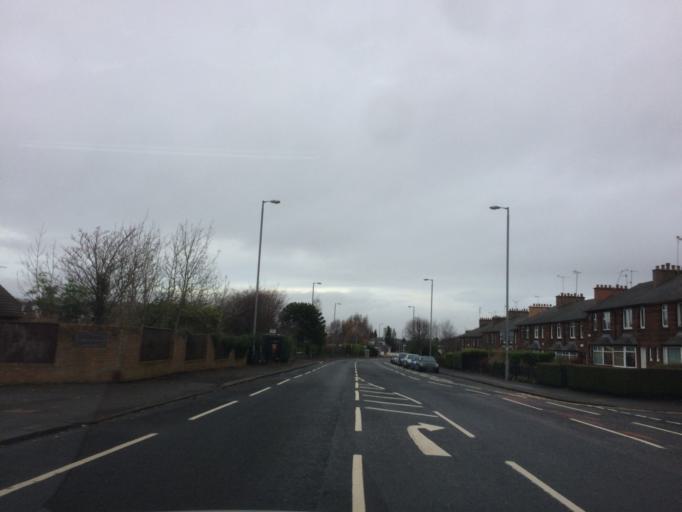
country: GB
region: Scotland
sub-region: East Renfrewshire
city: Giffnock
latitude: 55.8091
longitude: -4.2939
